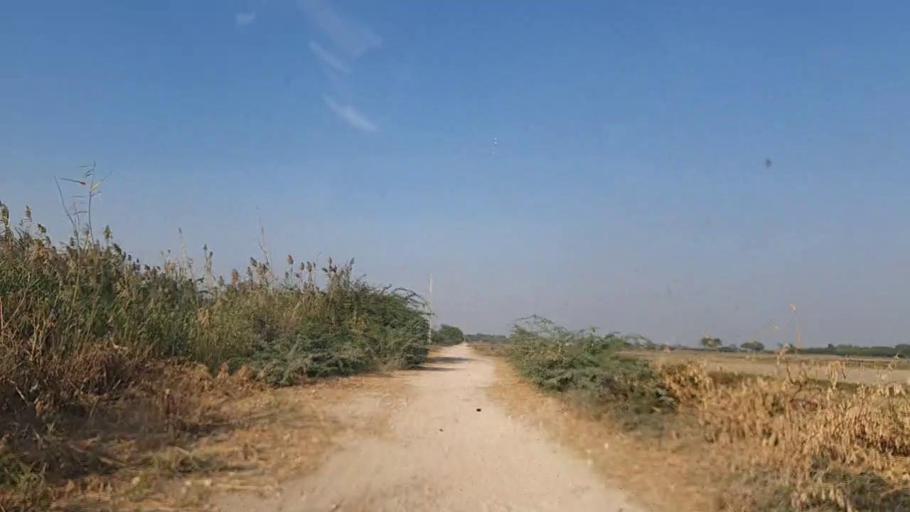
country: PK
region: Sindh
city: Thatta
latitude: 24.7501
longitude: 67.9601
